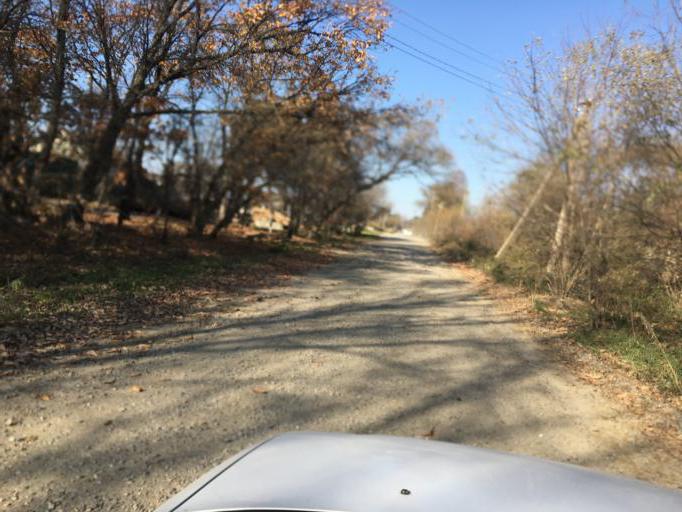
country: RU
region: Primorskiy
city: Dal'nerechensk
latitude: 45.9173
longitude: 133.7156
